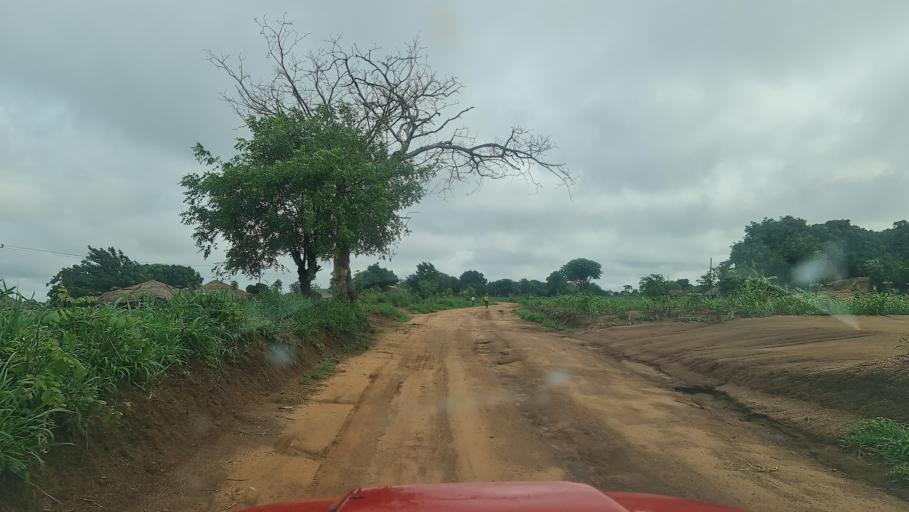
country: MW
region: Southern Region
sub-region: Nsanje District
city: Nsanje
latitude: -17.2055
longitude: 35.6824
